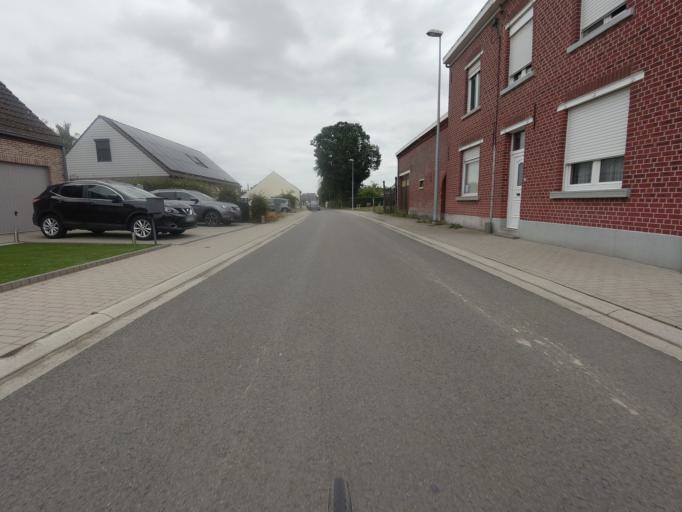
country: BE
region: Flanders
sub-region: Provincie Vlaams-Brabant
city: Herent
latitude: 50.9273
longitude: 4.6281
